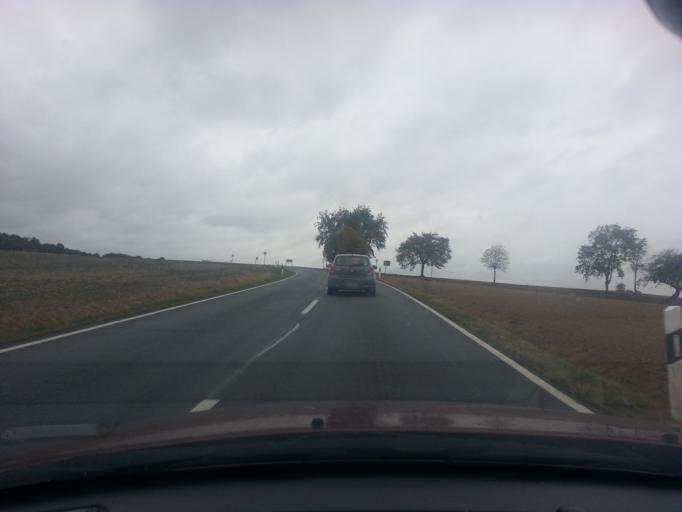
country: DE
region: Saxony
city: Markersdorf
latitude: 51.1117
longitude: 14.9174
